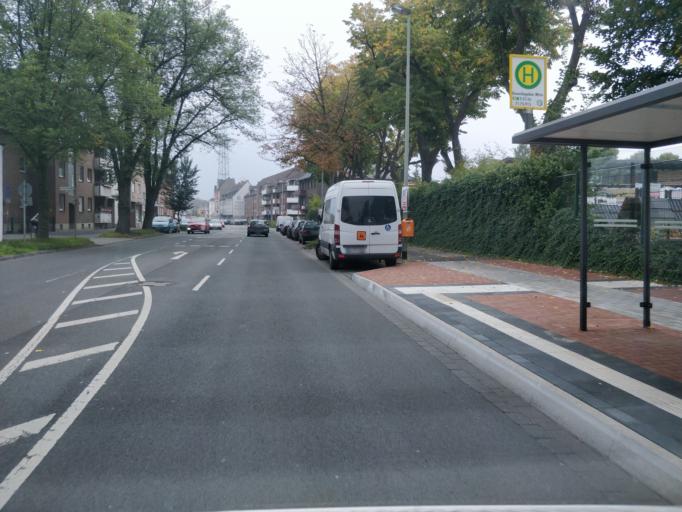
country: DE
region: North Rhine-Westphalia
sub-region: Regierungsbezirk Dusseldorf
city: Dinslaken
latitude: 51.5675
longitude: 6.7473
